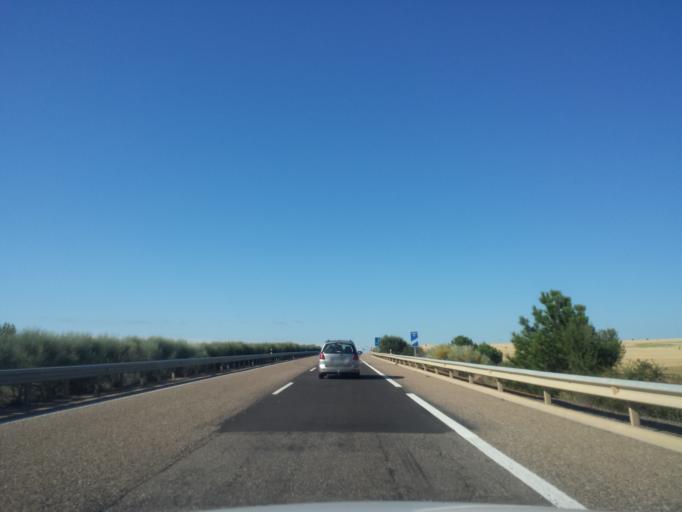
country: ES
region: Castille and Leon
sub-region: Provincia de Zamora
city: Matilla de Arzon
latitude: 42.1318
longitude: -5.6458
